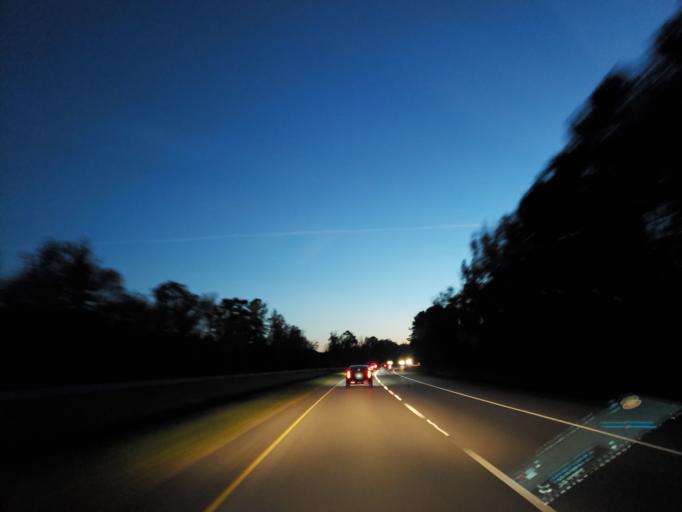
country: US
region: Mississippi
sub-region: Clarke County
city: Stonewall
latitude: 32.2199
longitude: -88.8339
